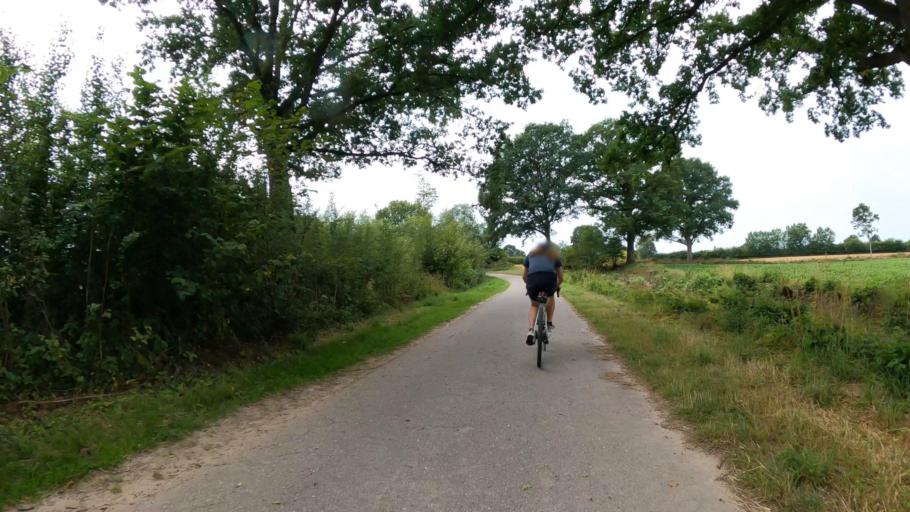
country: DE
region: Schleswig-Holstein
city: Fredesdorf
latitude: 53.8598
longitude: 10.2186
